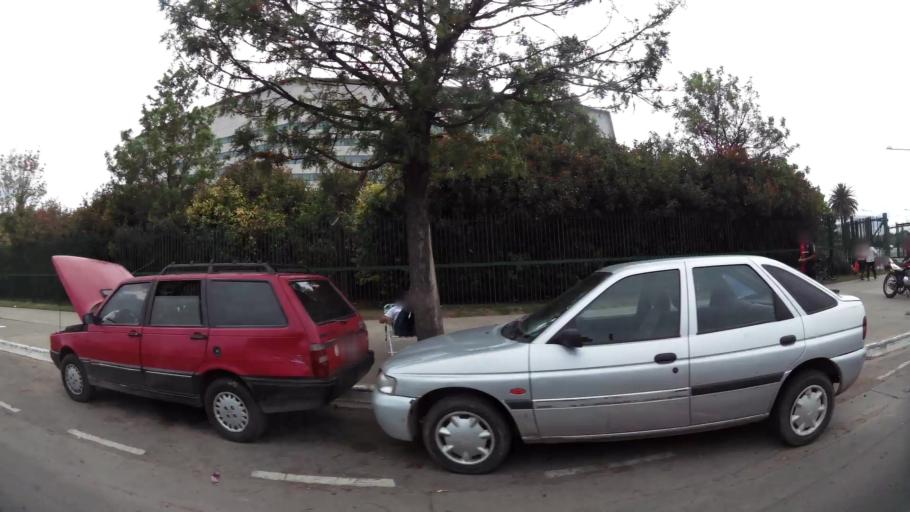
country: AR
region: Santa Fe
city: Gobernador Galvez
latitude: -33.0094
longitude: -60.6627
